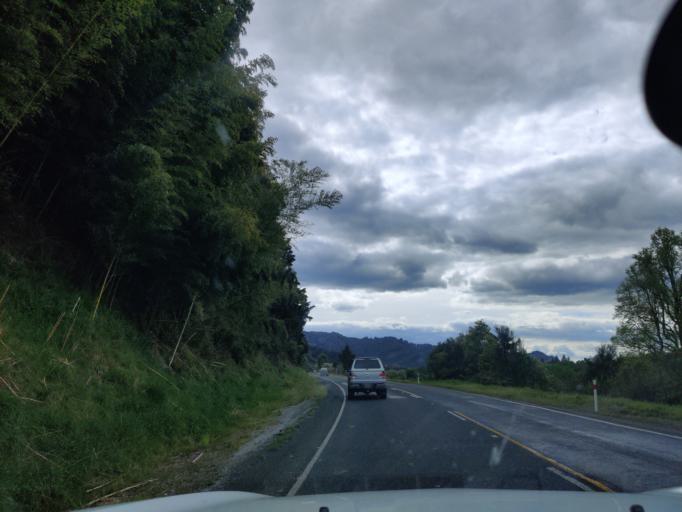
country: NZ
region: Waikato
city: Turangi
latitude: -38.8698
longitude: 175.2456
